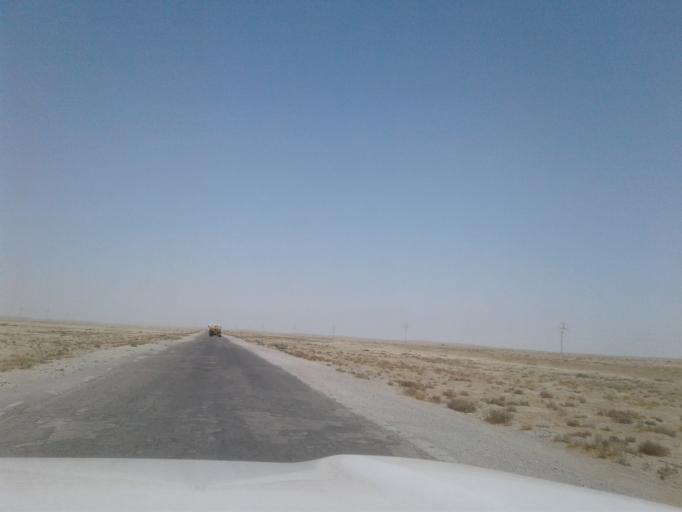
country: TM
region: Balkan
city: Gumdag
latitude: 38.3457
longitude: 54.3653
